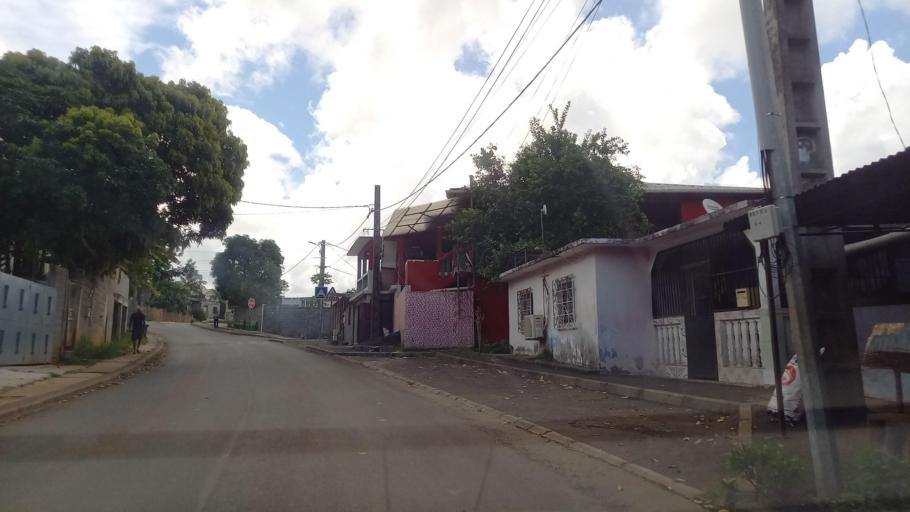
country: YT
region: Chirongui
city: Chirongui
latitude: -12.8910
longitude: 45.1393
